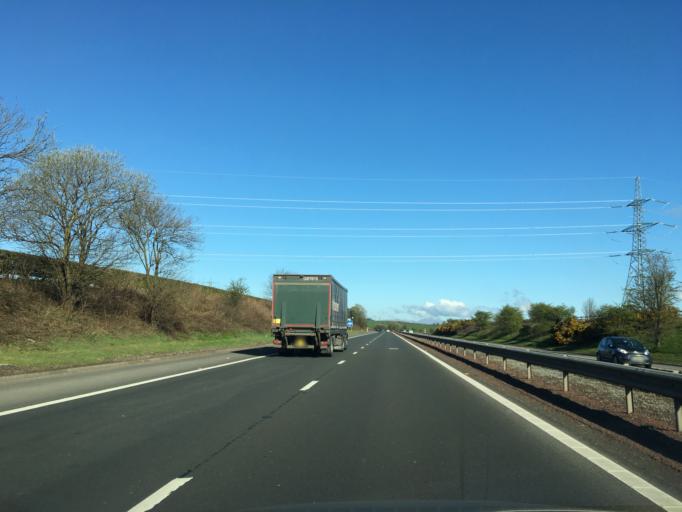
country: GB
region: Scotland
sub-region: Stirling
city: Cowie
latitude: 56.0589
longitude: -3.8544
